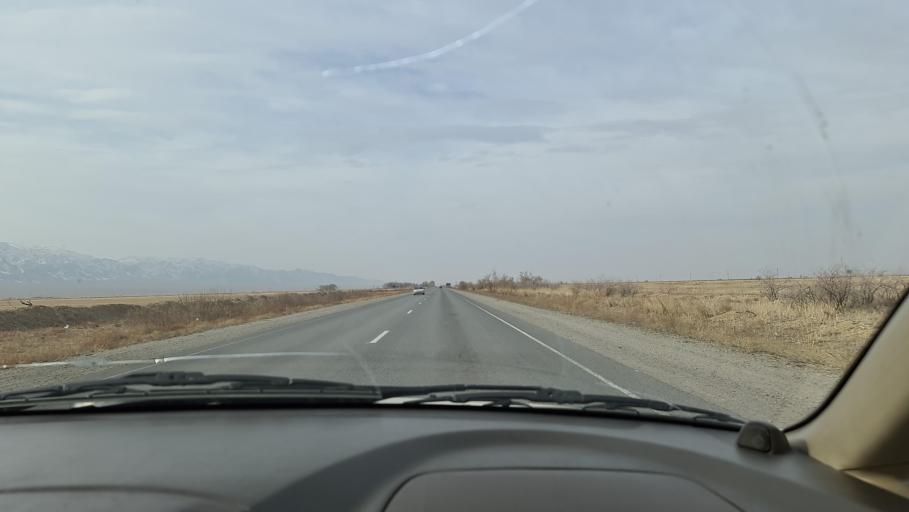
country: KG
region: Chuy
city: Tokmok
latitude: 43.3479
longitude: 75.4972
